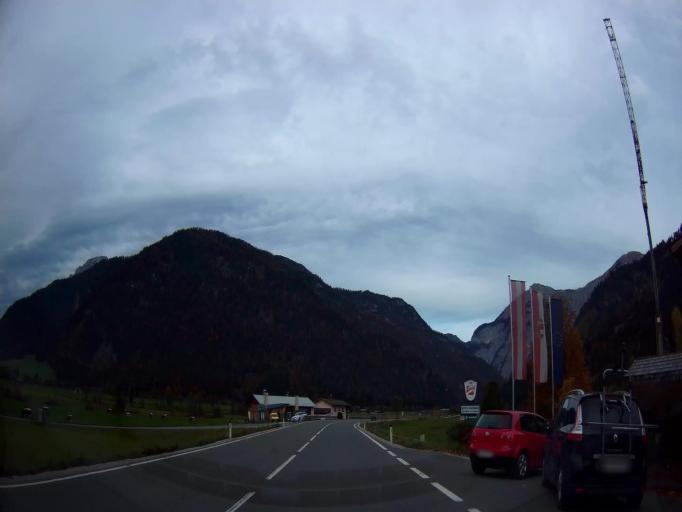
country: AT
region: Salzburg
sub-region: Politischer Bezirk Zell am See
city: Saalfelden am Steinernen Meer
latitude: 47.4543
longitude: 12.8315
